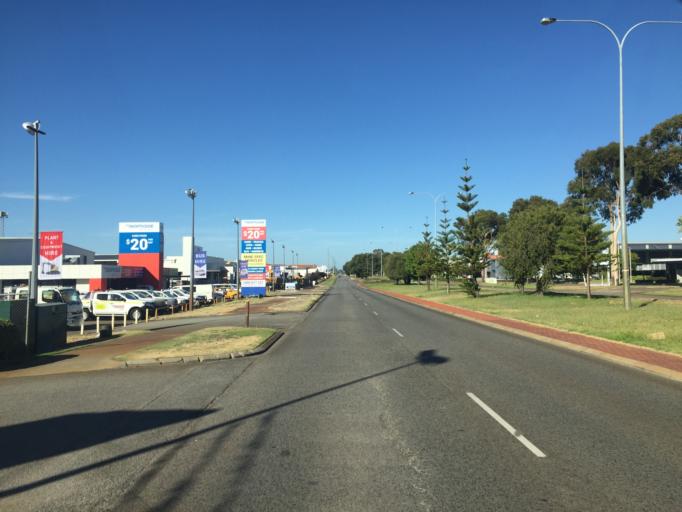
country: AU
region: Western Australia
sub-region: Belmont
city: Kewdale
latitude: -31.9897
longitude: 115.9477
